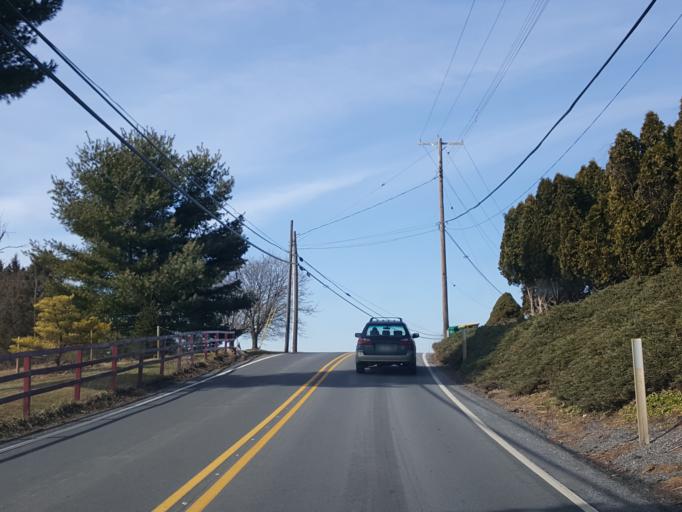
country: US
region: Pennsylvania
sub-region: Lebanon County
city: Campbelltown
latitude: 40.2714
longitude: -76.5662
